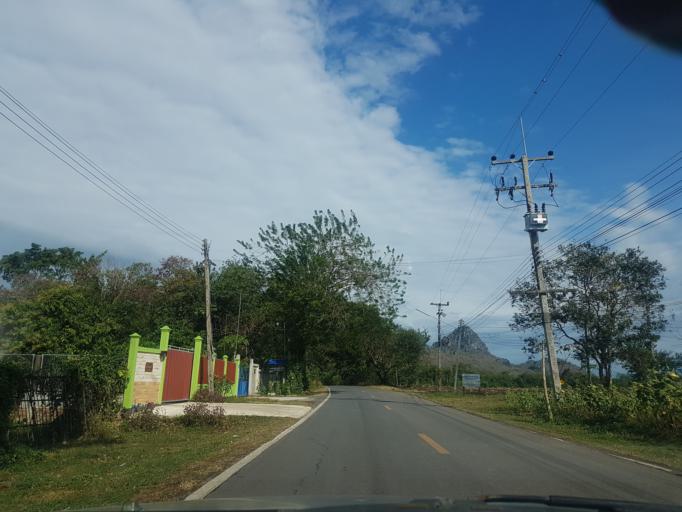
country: TH
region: Sara Buri
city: Phra Phutthabat
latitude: 14.8071
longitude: 100.7525
